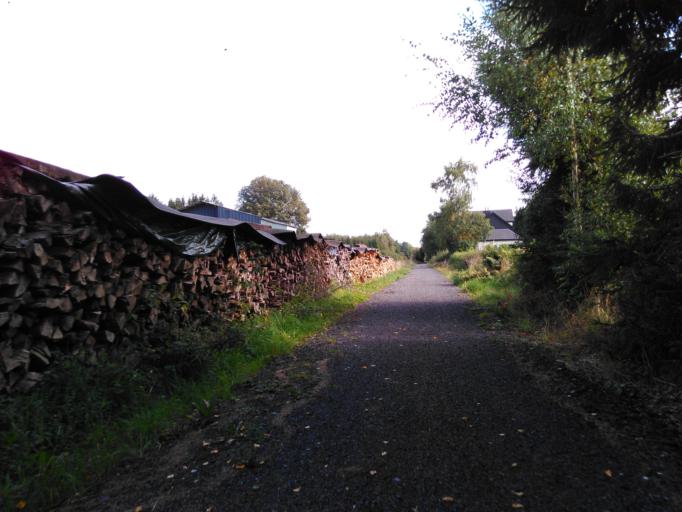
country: BE
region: Wallonia
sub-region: Province du Luxembourg
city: Vaux-sur-Sure
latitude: 49.9477
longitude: 5.5999
